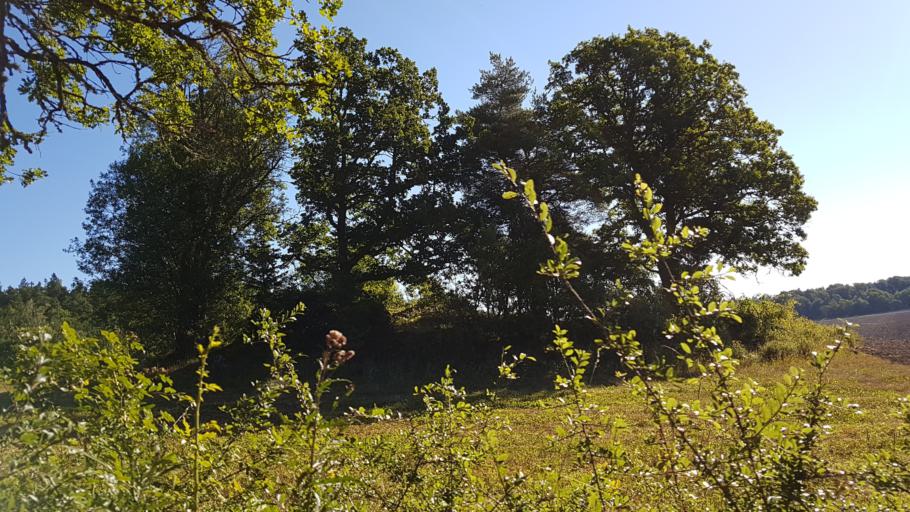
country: SE
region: OEstergoetland
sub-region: Valdemarsviks Kommun
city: Gusum
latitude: 58.4299
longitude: 16.5753
